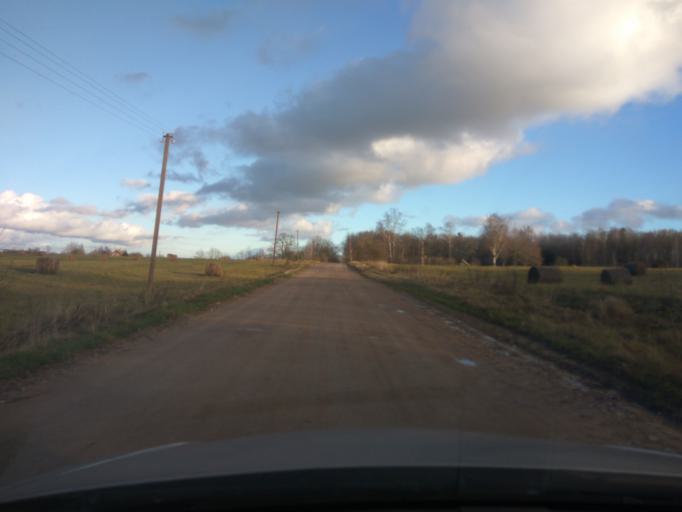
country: LV
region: Aizpute
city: Aizpute
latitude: 56.7479
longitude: 21.5932
